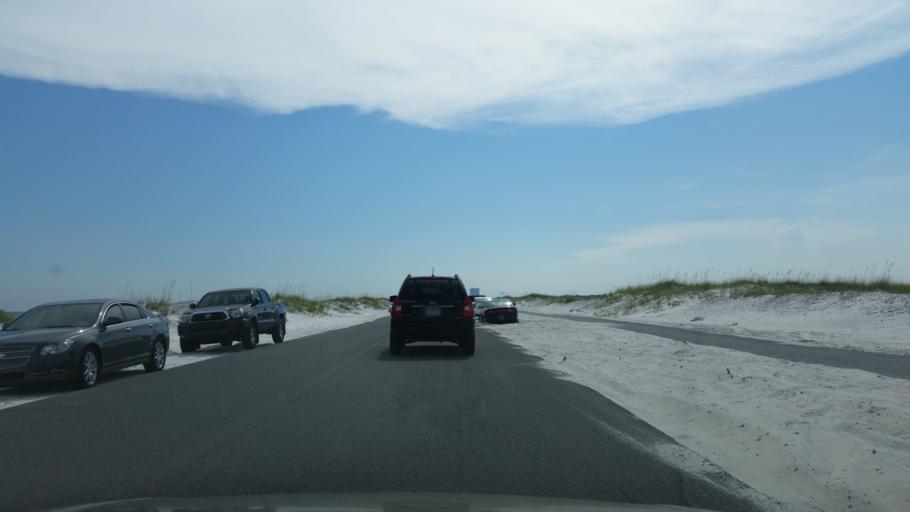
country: US
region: Florida
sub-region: Santa Rosa County
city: Tiger Point
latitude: 30.3510
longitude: -87.0368
